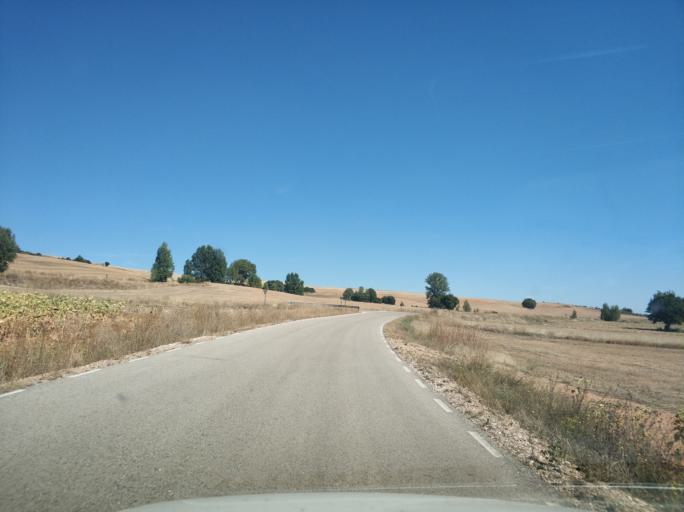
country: ES
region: Castille and Leon
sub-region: Provincia de Soria
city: Fuentearmegil
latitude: 41.6988
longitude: -3.2195
